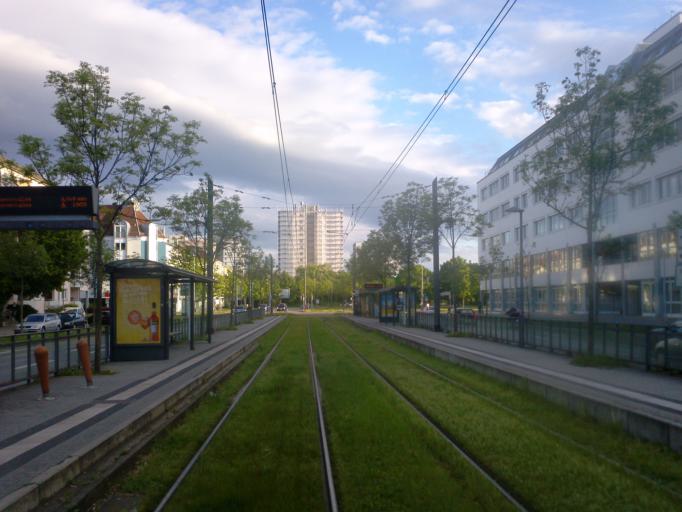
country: DE
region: Baden-Wuerttemberg
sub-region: Karlsruhe Region
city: Karlsruhe
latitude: 48.9996
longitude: 8.3860
